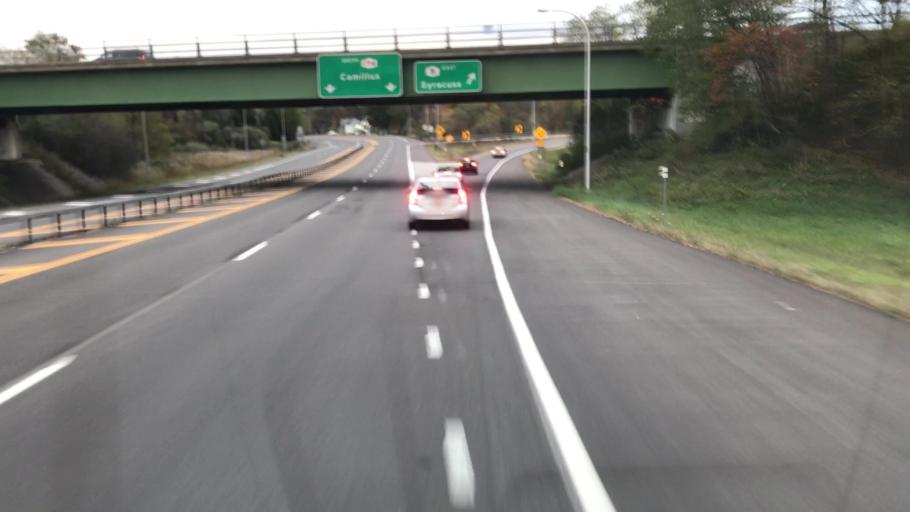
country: US
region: New York
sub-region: Onondaga County
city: Camillus
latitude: 43.0352
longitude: -76.3233
